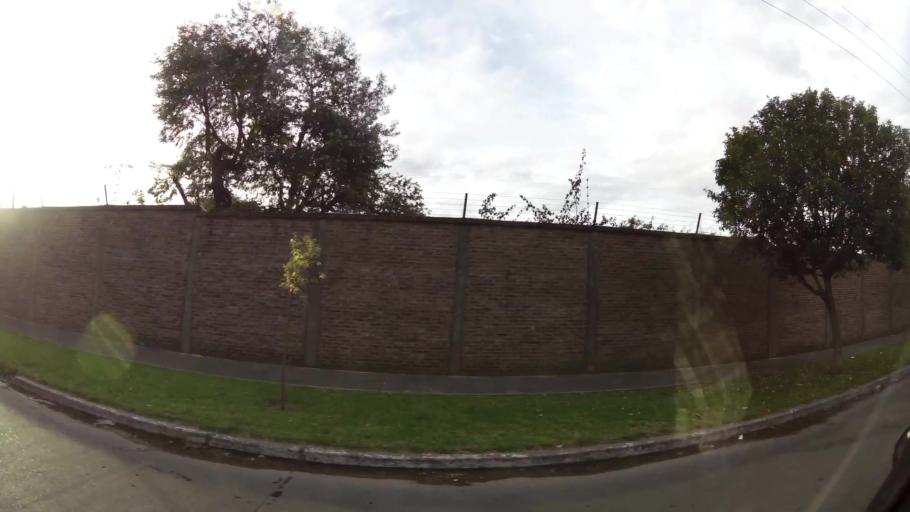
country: AR
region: Buenos Aires
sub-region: Partido de Quilmes
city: Quilmes
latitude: -34.7220
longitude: -58.2389
